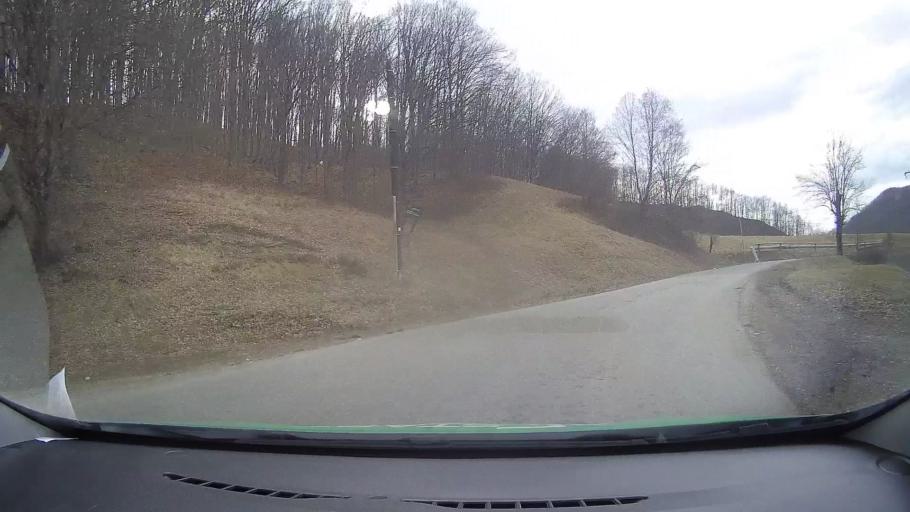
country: RO
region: Dambovita
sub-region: Comuna Visinesti
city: Visinesti
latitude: 45.0978
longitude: 25.5794
